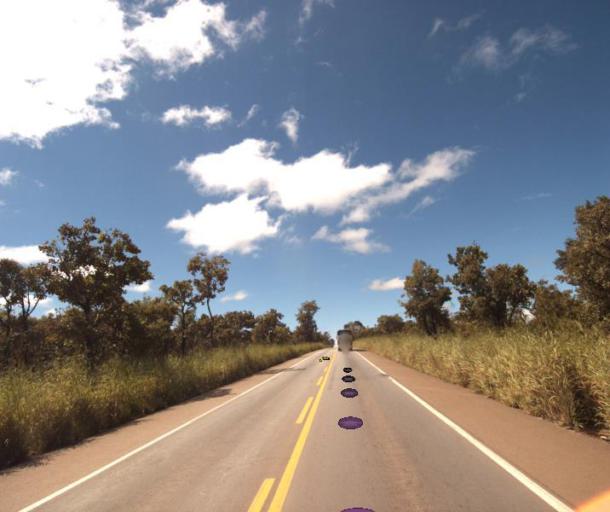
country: BR
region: Goias
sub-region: Uruana
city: Uruana
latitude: -15.5184
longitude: -49.4692
